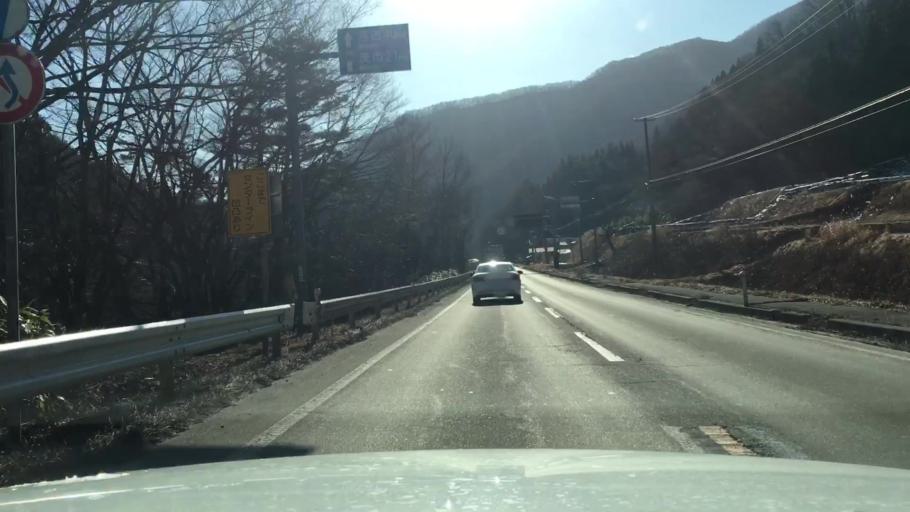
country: JP
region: Iwate
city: Tono
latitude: 39.6189
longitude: 141.6229
